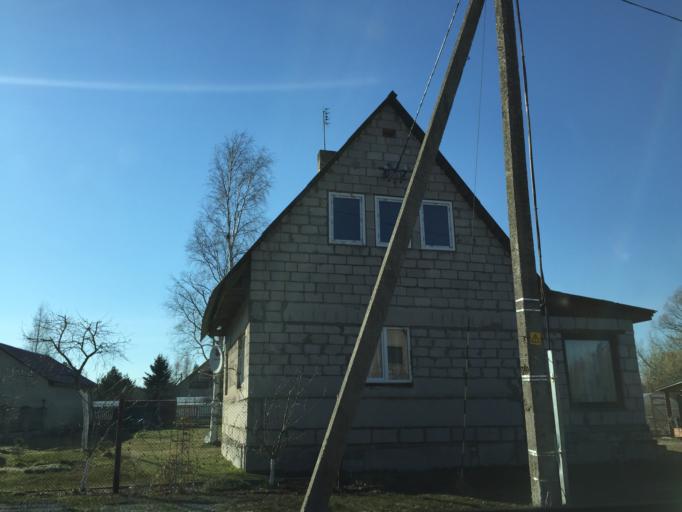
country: RU
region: Pskov
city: Gdov
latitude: 58.9999
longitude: 27.7357
